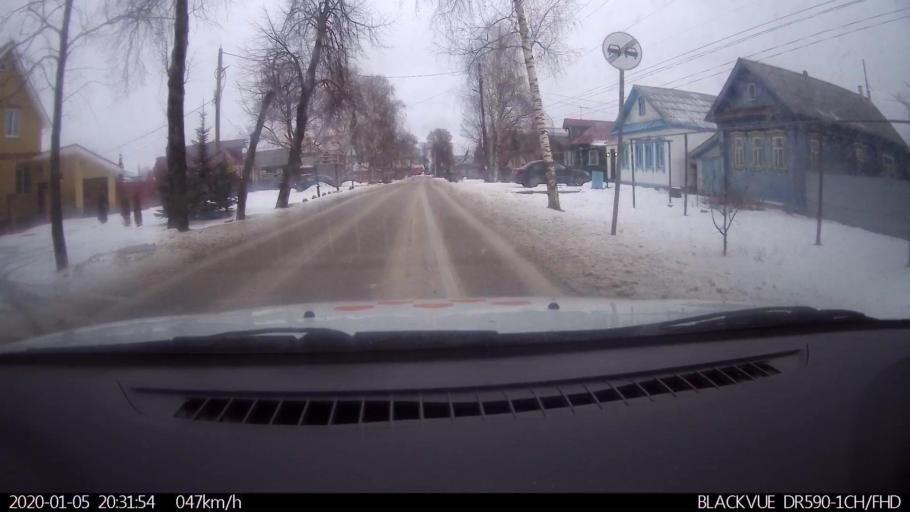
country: RU
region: Nizjnij Novgorod
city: Lukino
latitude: 56.4093
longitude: 43.7286
